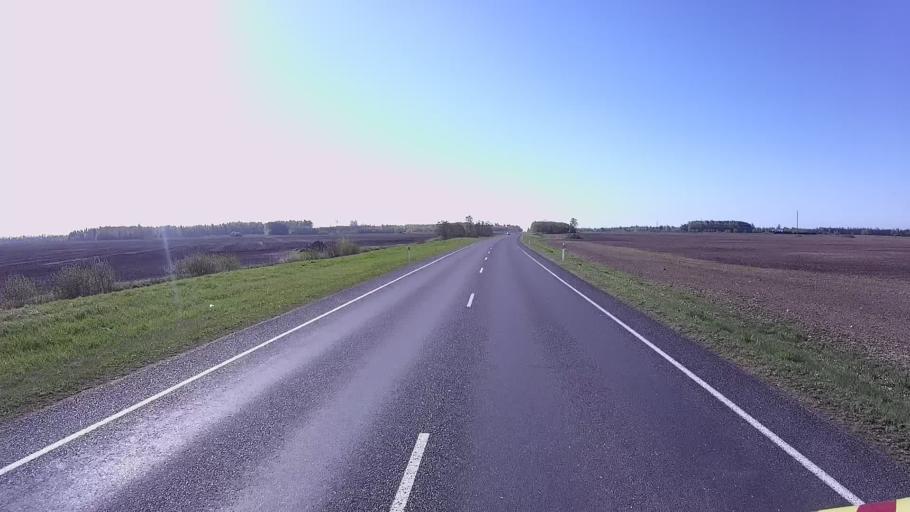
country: EE
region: Viljandimaa
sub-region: Vohma linn
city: Vohma
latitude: 58.7385
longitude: 25.5852
